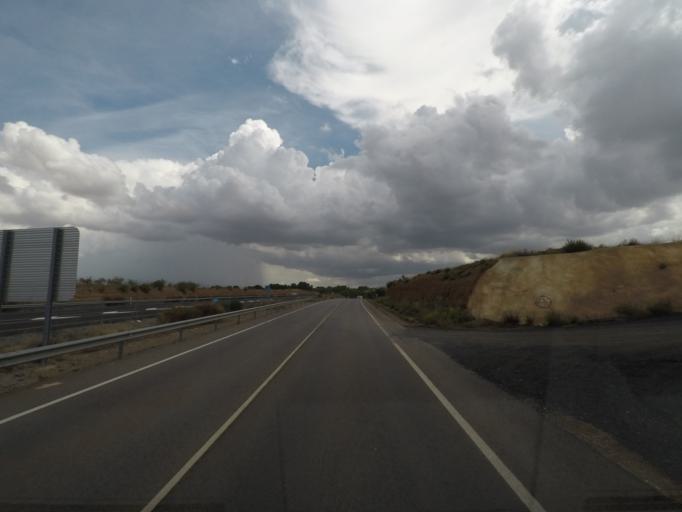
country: ES
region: Andalusia
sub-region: Provincia de Granada
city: Albunan
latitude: 37.2643
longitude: -3.0894
